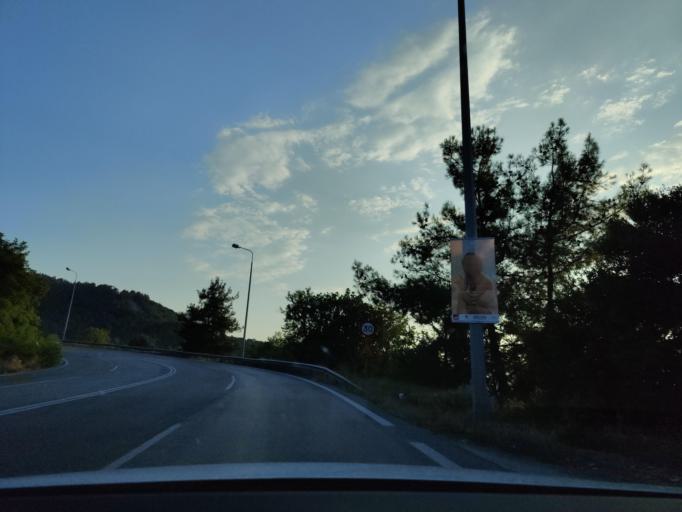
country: GR
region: East Macedonia and Thrace
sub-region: Nomos Kavalas
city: Amygdaleonas
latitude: 40.9499
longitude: 24.3706
